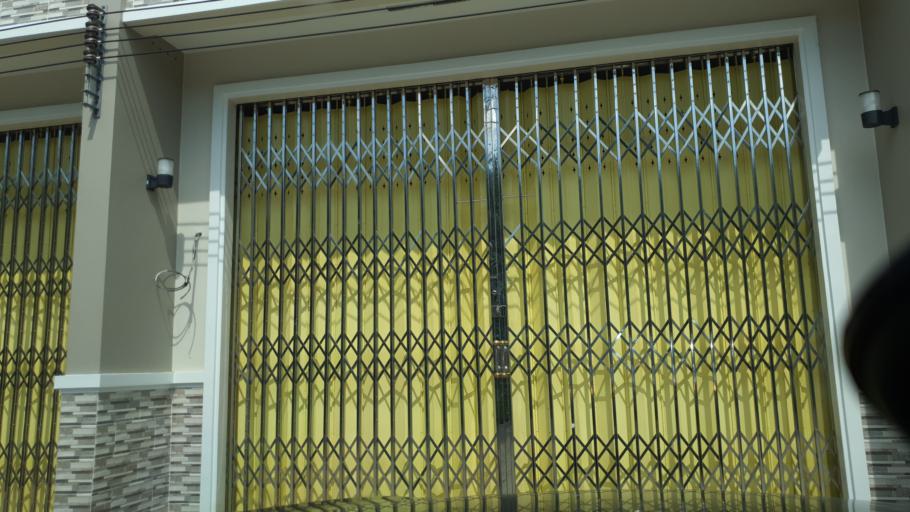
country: TH
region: Krabi
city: Nuea Khlong
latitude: 8.0839
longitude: 98.9874
